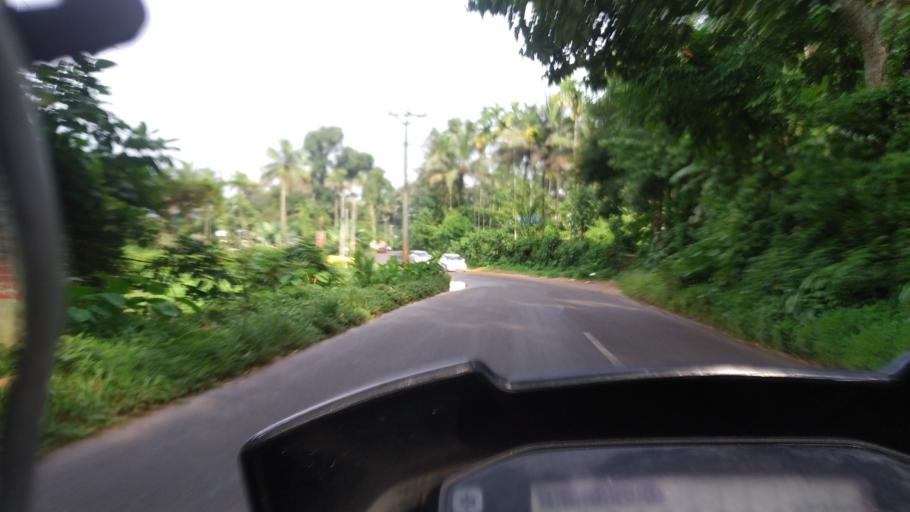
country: IN
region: Kerala
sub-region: Ernakulam
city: Kotamangalam
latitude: 10.0515
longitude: 76.7085
